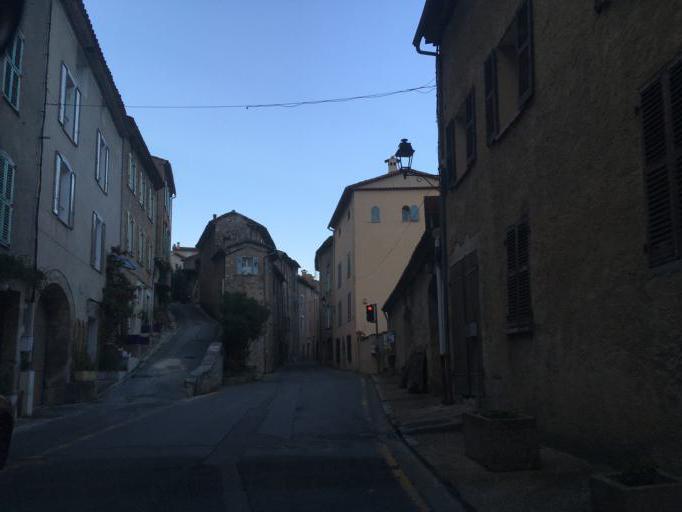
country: FR
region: Provence-Alpes-Cote d'Azur
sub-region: Departement du Var
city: Salernes
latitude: 43.5134
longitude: 6.2423
